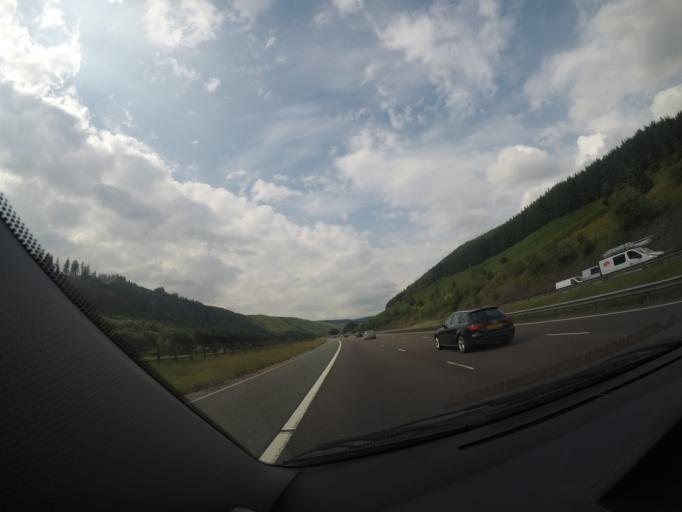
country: GB
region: Scotland
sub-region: Dumfries and Galloway
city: Moffat
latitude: 55.3752
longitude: -3.5148
